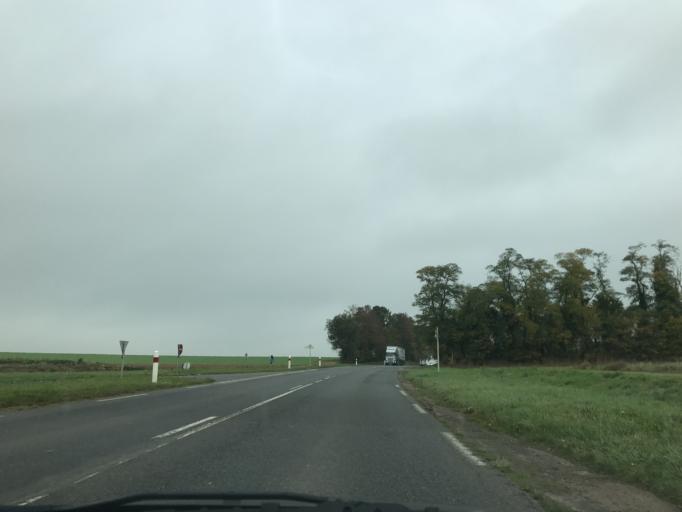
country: FR
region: Picardie
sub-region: Departement de la Somme
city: Peronne
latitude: 49.8991
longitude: 2.9230
